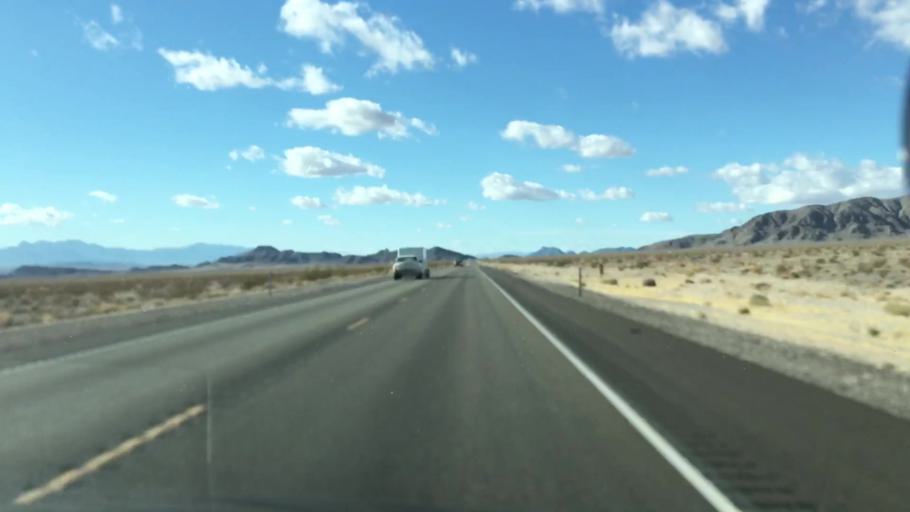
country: US
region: Nevada
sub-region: Nye County
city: Pahrump
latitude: 36.5698
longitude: -116.1580
